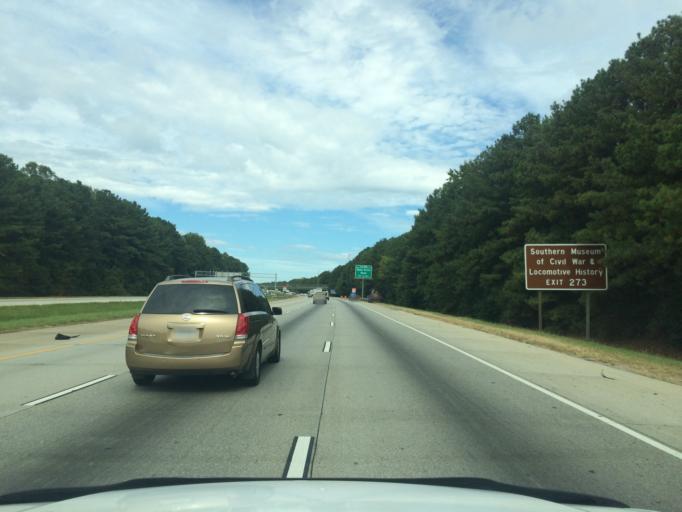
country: US
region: Georgia
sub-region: Cobb County
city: Kennesaw
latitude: 34.0454
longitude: -84.5823
